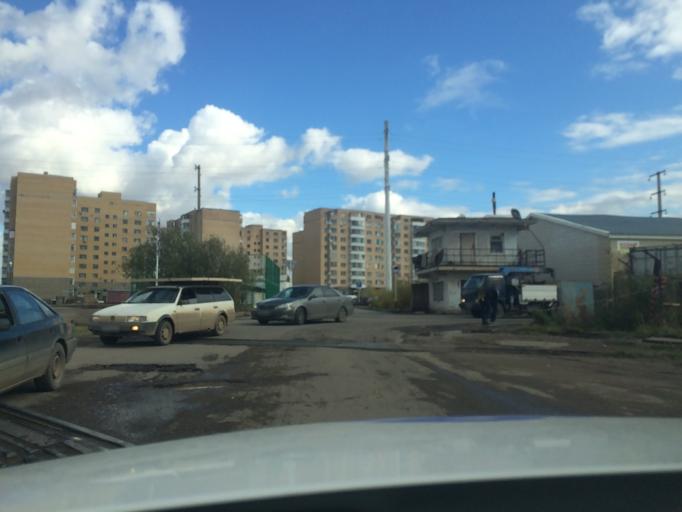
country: KZ
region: Astana Qalasy
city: Astana
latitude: 51.1840
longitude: 71.4356
